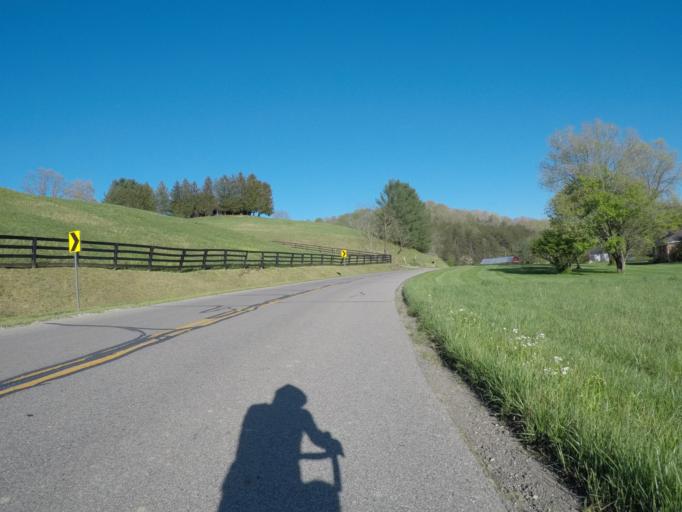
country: US
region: Kentucky
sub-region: Boyd County
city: Meads
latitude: 38.3666
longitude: -82.6811
